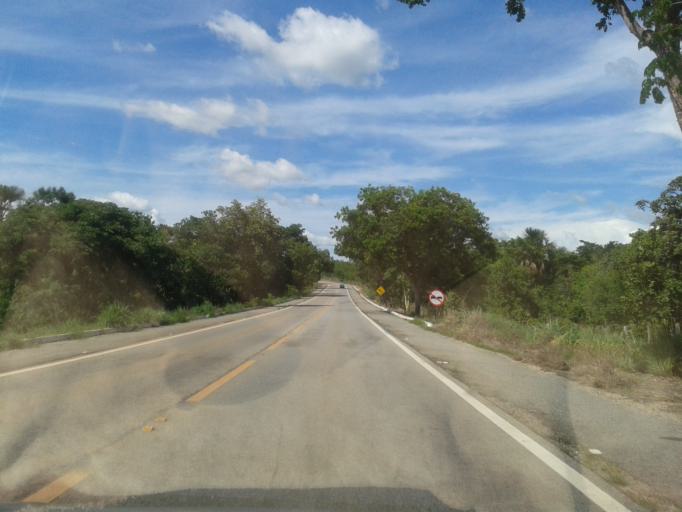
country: BR
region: Goias
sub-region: Itapuranga
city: Itapuranga
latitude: -15.3782
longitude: -50.3883
